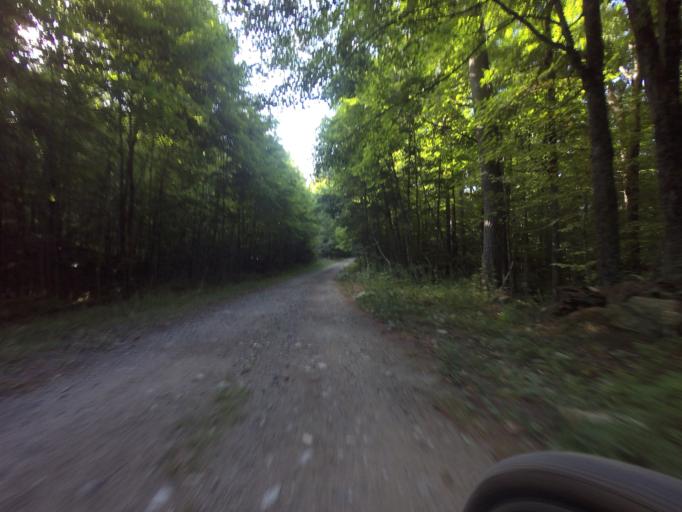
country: CA
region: Ontario
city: Arnprior
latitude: 45.1890
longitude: -76.5144
